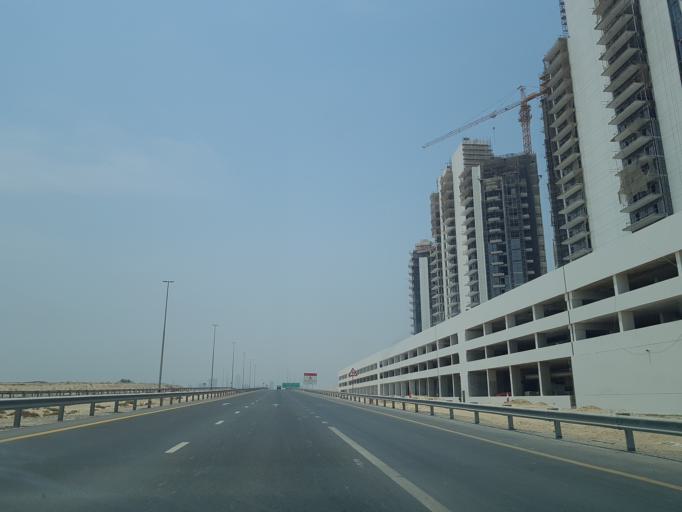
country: AE
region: Dubai
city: Dubai
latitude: 25.0181
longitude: 55.2455
